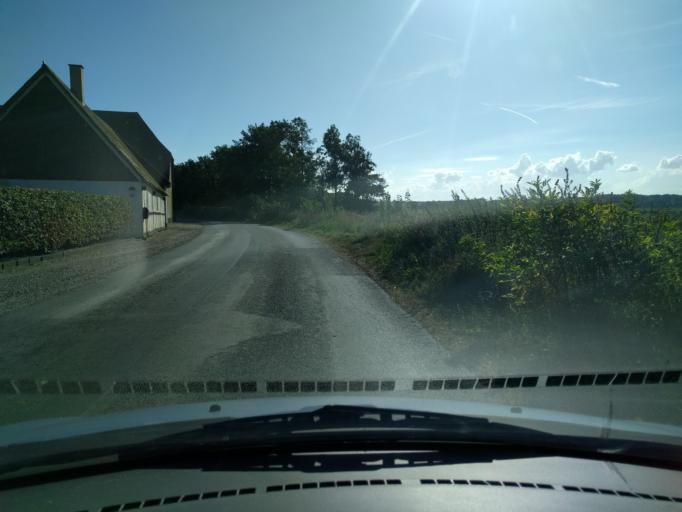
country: DK
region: South Denmark
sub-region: Assens Kommune
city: Harby
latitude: 55.1457
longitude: 10.0198
